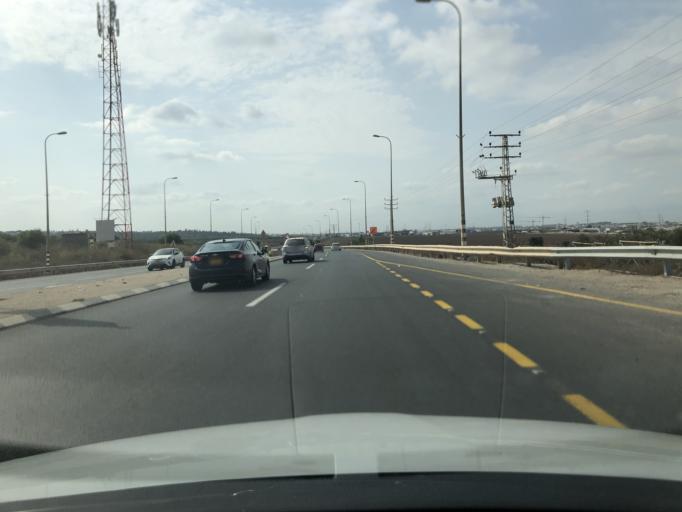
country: IL
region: Central District
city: Et Taiyiba
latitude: 32.2415
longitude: 34.9895
